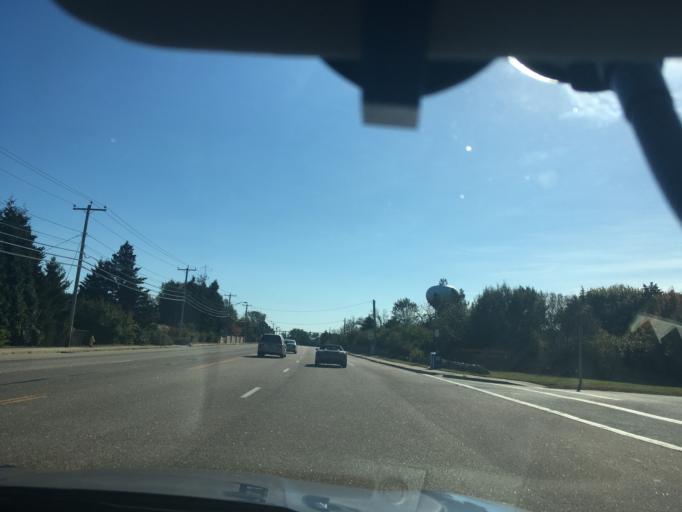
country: US
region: Rhode Island
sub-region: Washington County
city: Narragansett Pier
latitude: 41.3803
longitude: -71.4882
